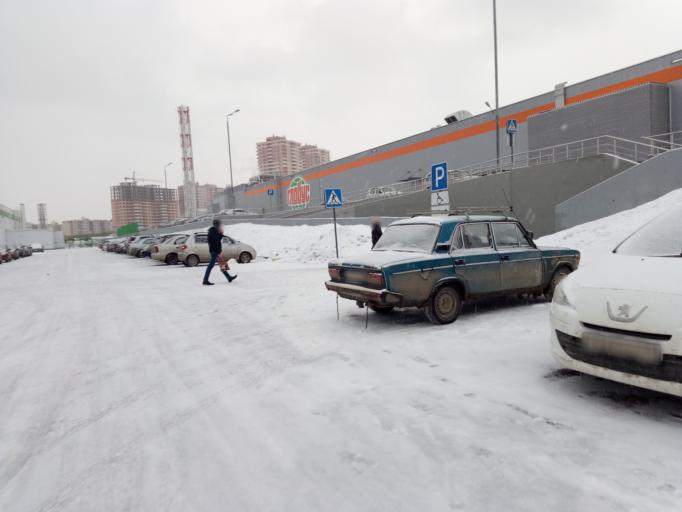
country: RU
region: Tula
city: Tula
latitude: 54.1775
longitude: 37.6473
